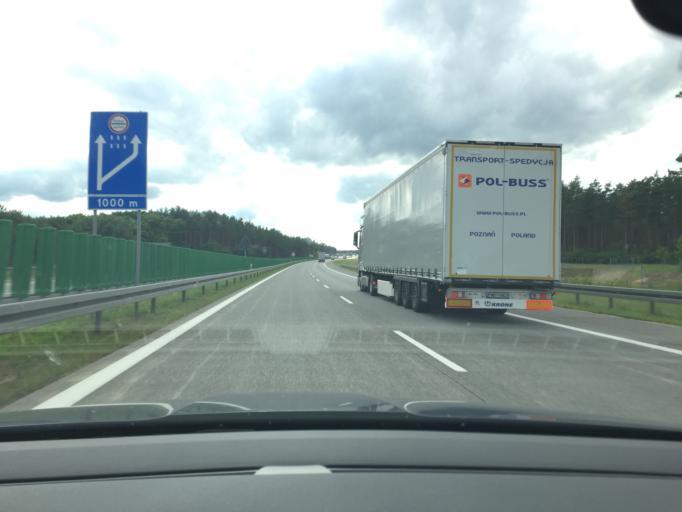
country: PL
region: Lubusz
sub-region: Powiat slubicki
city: Rzepin
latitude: 52.3340
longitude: 14.9193
